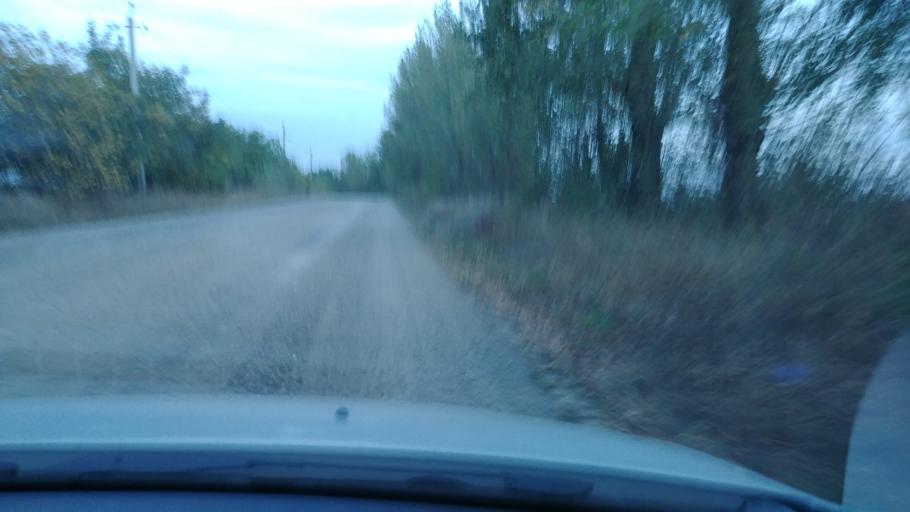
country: MD
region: Rezina
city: Saharna
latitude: 47.6805
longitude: 28.9170
